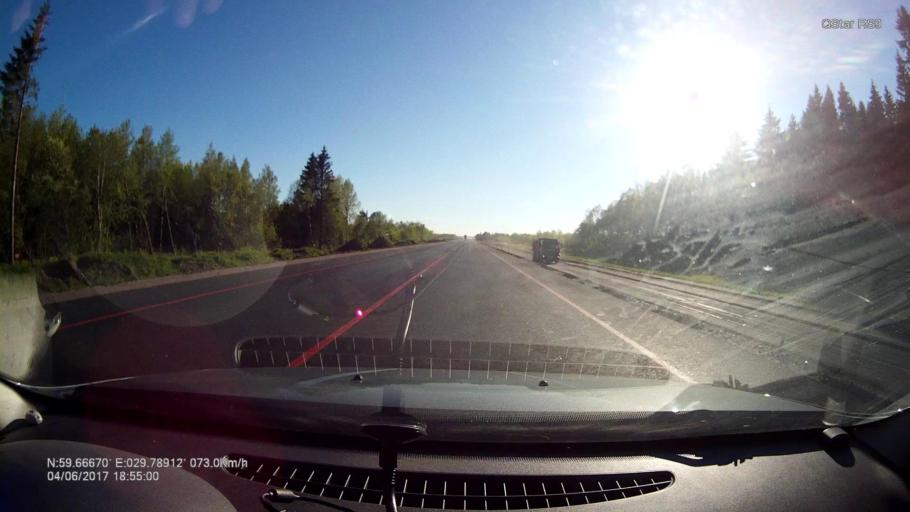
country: RU
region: Leningrad
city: Kipen'
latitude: 59.6667
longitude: 29.7890
